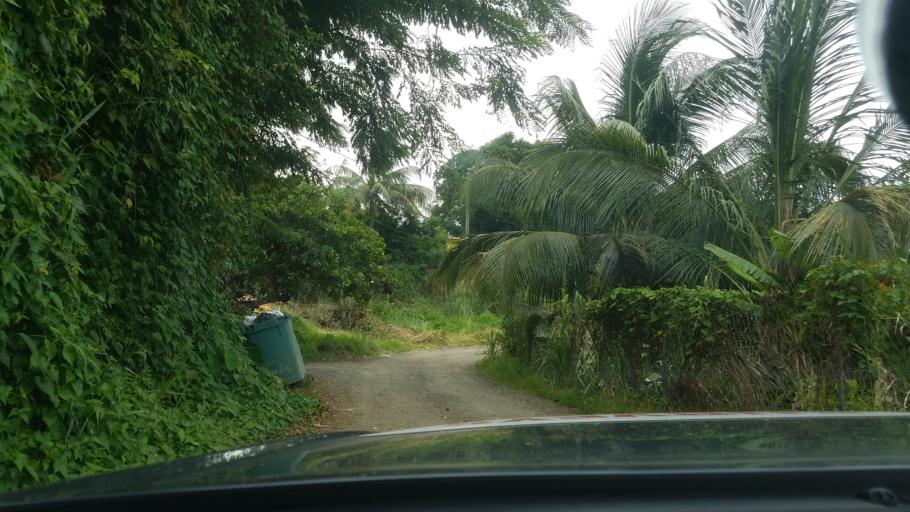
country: LC
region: Gros-Islet
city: Gros Islet
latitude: 14.0631
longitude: -60.9605
